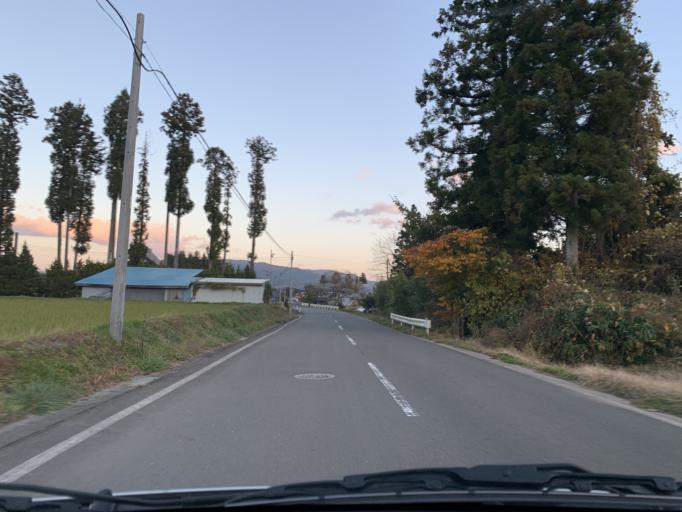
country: JP
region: Iwate
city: Ichinoseki
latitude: 39.0135
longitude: 141.0808
